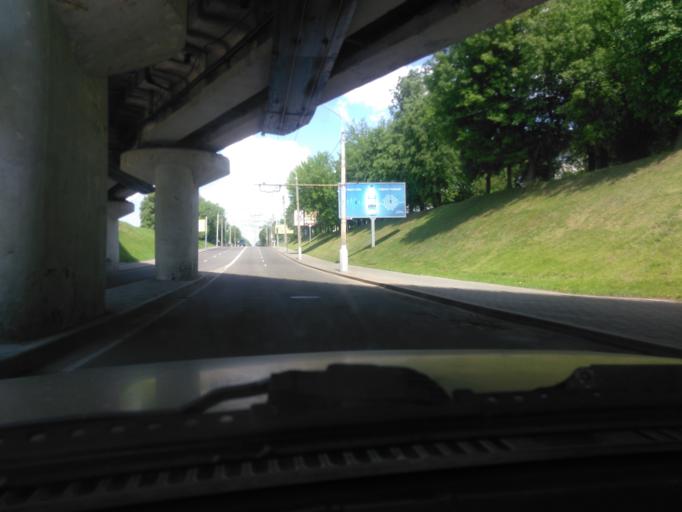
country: BY
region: Mogilev
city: Mahilyow
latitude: 53.9224
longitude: 30.3424
